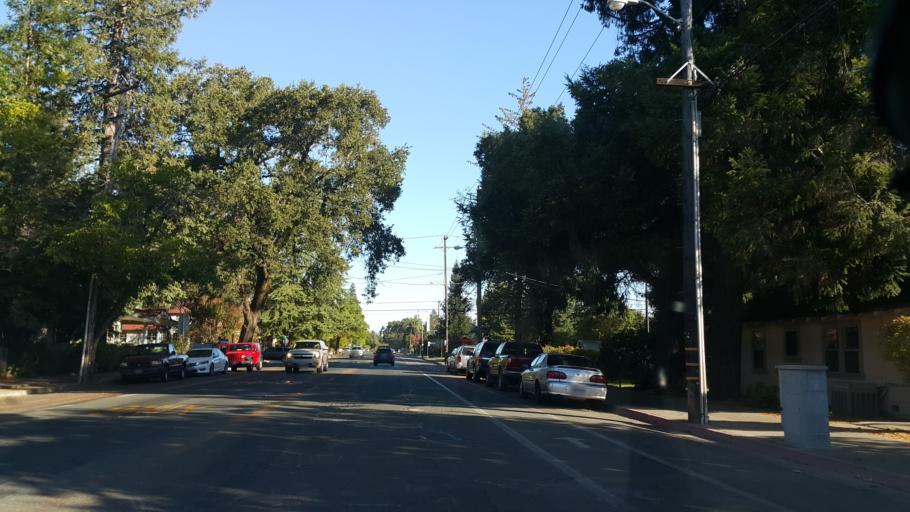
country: US
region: California
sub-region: Mendocino County
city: Ukiah
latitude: 39.1466
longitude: -123.2117
